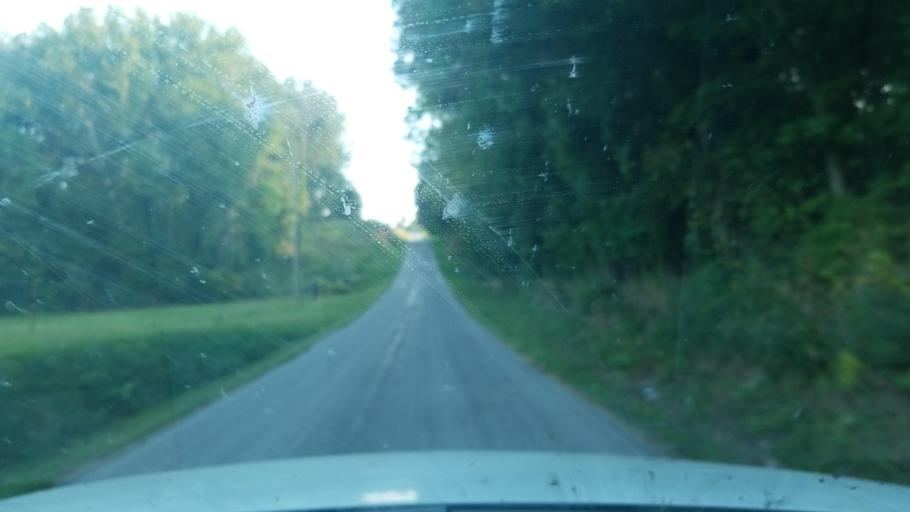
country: US
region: Illinois
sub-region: Saline County
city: Harrisburg
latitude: 37.8098
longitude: -88.6156
